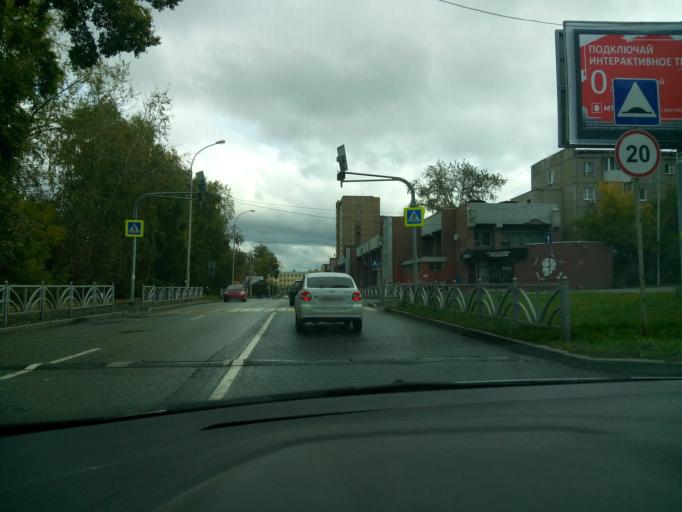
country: RU
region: Sverdlovsk
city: Yekaterinburg
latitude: 56.8169
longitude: 60.6011
